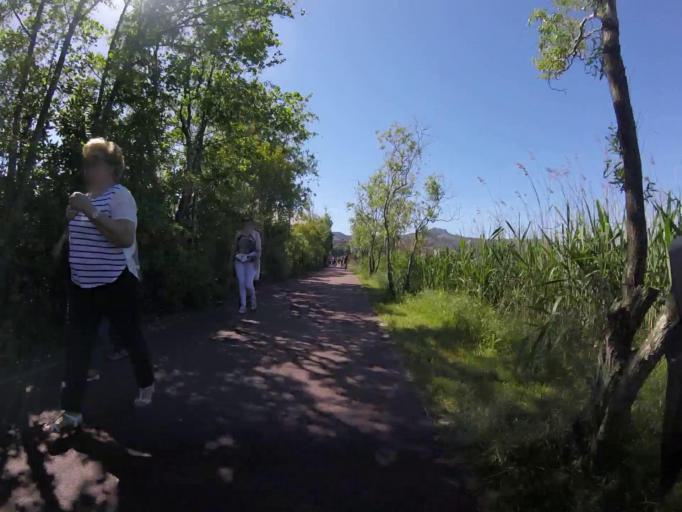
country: ES
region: Basque Country
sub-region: Provincia de Guipuzcoa
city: Irun
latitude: 43.3461
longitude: -1.7766
